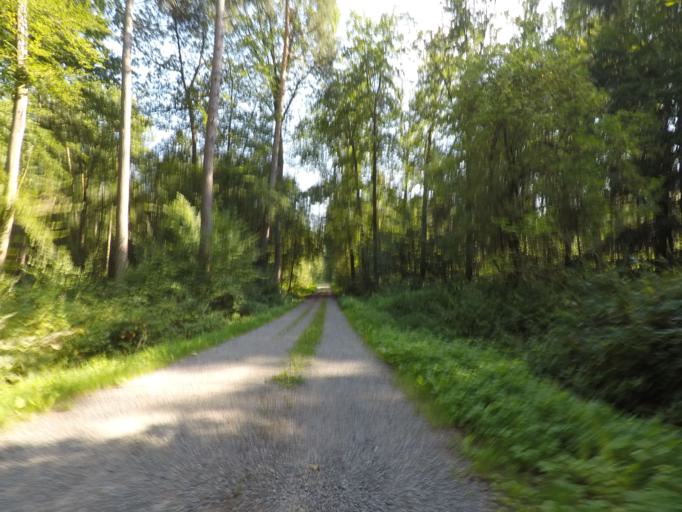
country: DE
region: Baden-Wuerttemberg
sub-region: Regierungsbezirk Stuttgart
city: Ehningen
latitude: 48.6667
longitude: 8.9774
